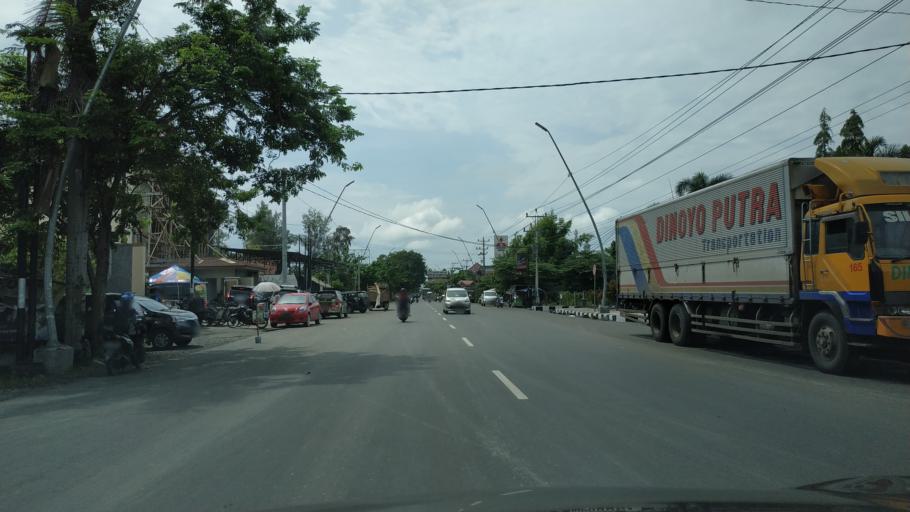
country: ID
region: Central Java
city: Tegal
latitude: -6.8783
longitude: 109.1269
